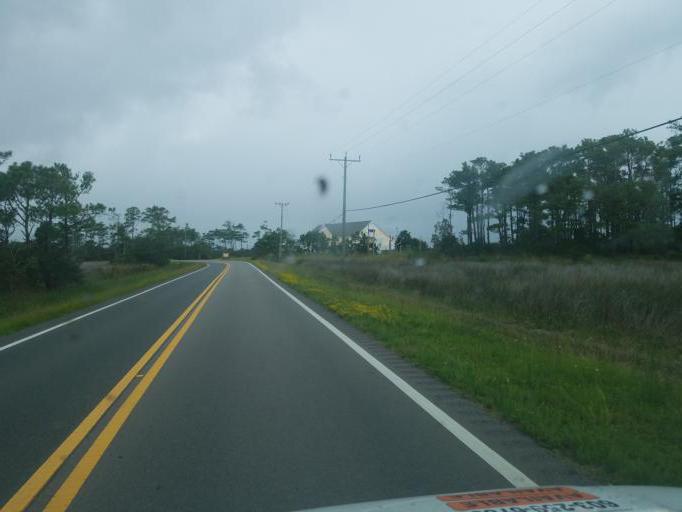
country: US
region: North Carolina
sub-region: Dare County
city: Wanchese
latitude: 35.8675
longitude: -75.6495
